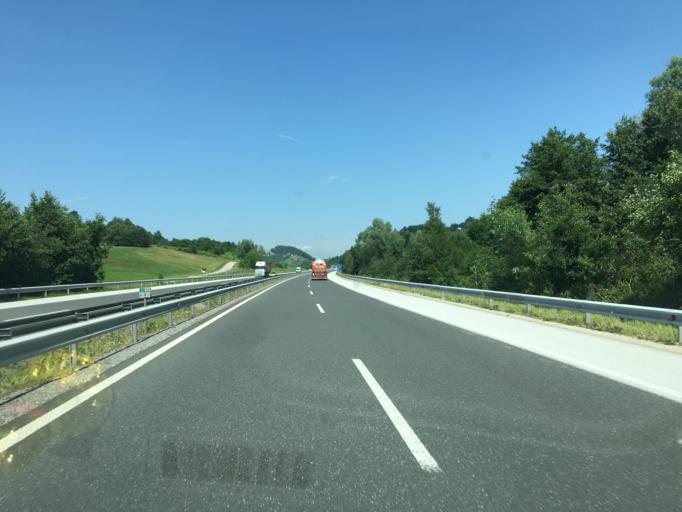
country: SI
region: Kungota
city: Zgornja Kungota
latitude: 46.6467
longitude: 15.6496
